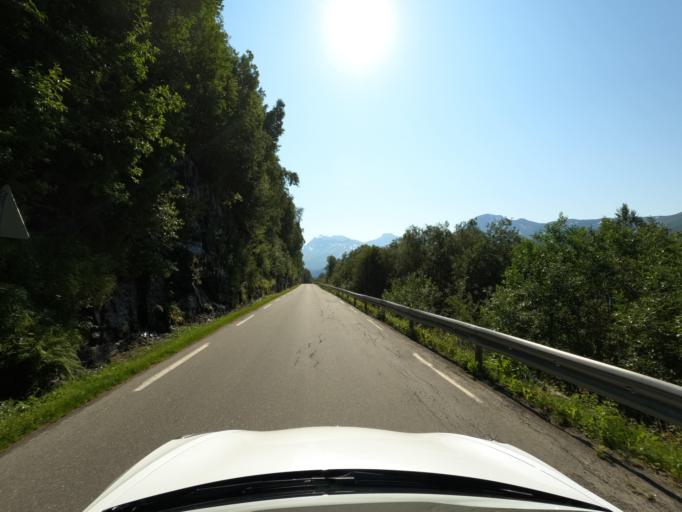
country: NO
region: Nordland
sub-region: Narvik
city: Narvik
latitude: 68.3457
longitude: 17.2792
